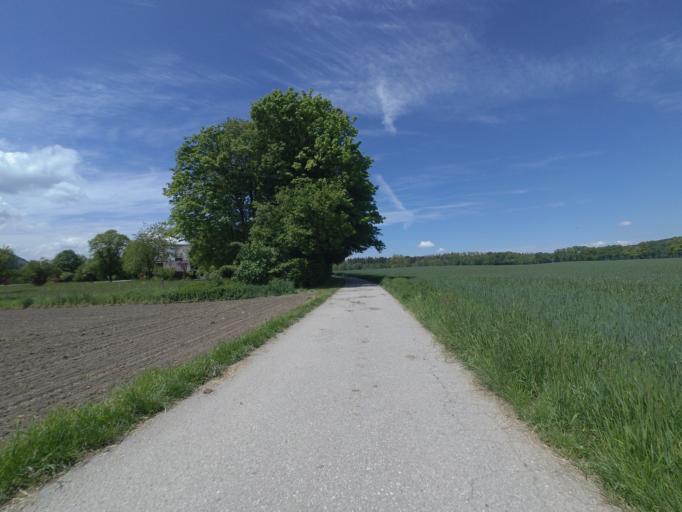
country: AT
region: Salzburg
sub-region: Politischer Bezirk Salzburg-Umgebung
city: Anif
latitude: 47.7554
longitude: 13.0549
